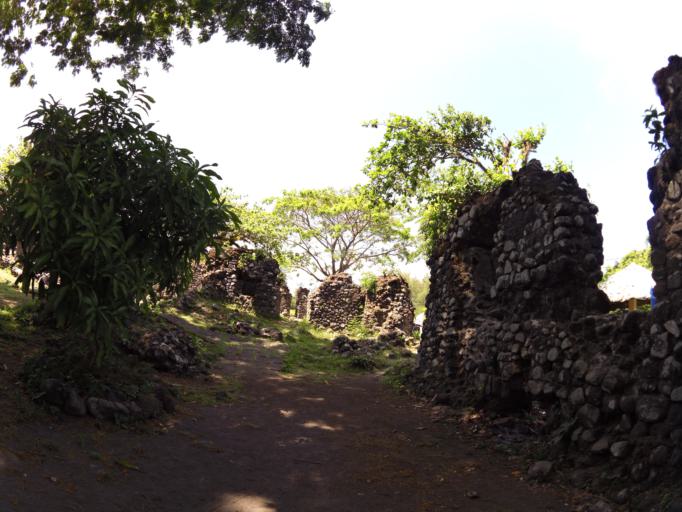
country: PH
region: Bicol
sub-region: Province of Albay
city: Tagas
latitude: 13.1661
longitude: 123.7013
